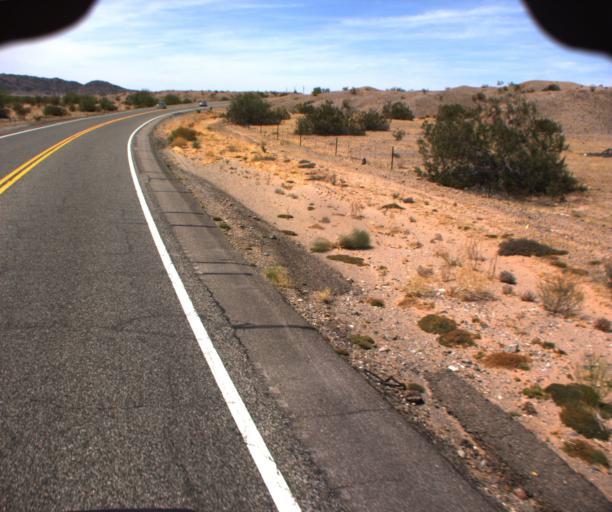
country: US
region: Arizona
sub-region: La Paz County
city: Parker
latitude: 33.9978
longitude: -114.2267
